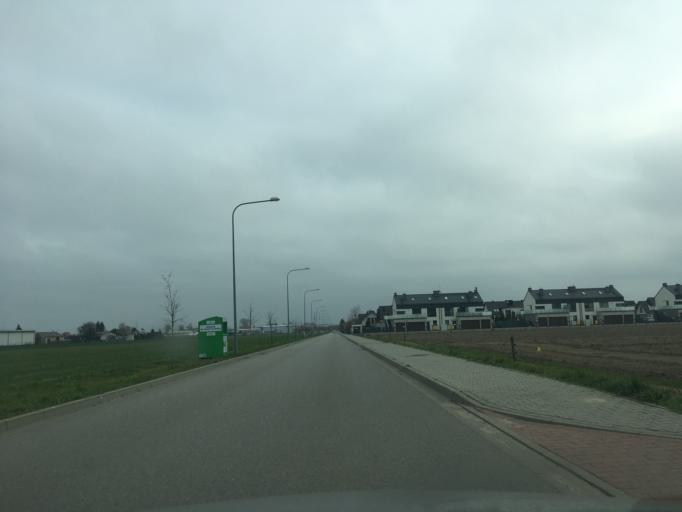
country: PL
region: Masovian Voivodeship
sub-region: Powiat piaseczynski
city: Lesznowola
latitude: 52.0835
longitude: 20.9497
